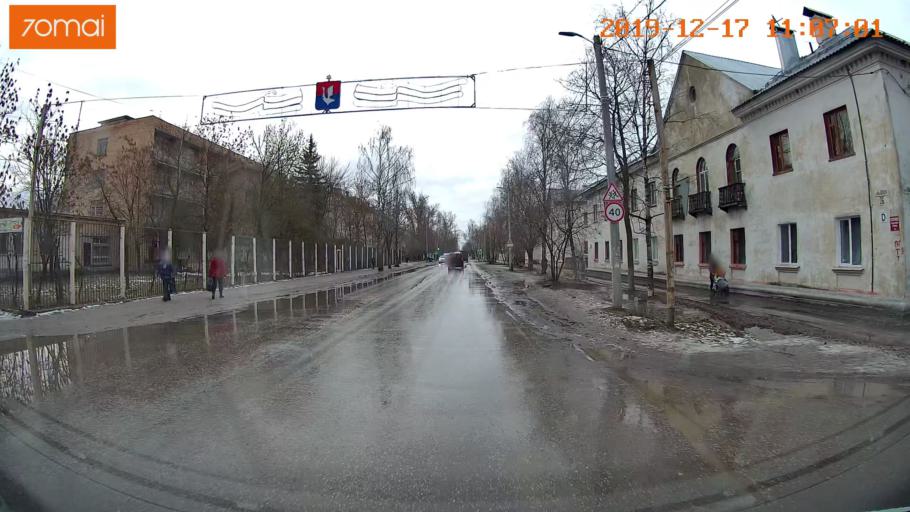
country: RU
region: Vladimir
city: Gus'-Khrustal'nyy
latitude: 55.6130
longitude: 40.6446
